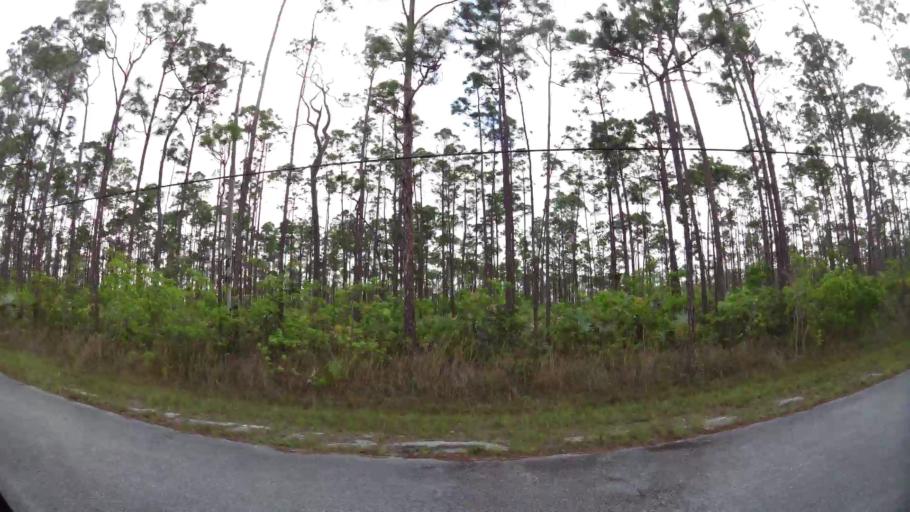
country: BS
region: Freeport
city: Lucaya
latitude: 26.5884
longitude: -78.5495
